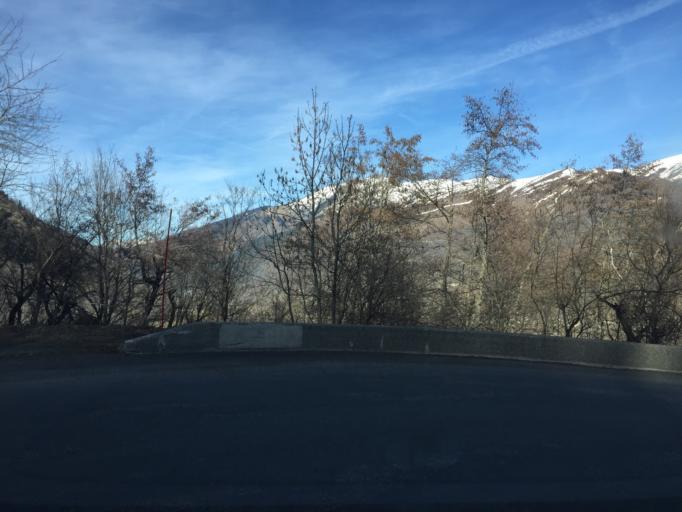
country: FR
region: Midi-Pyrenees
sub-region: Departement des Hautes-Pyrenees
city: Saint-Lary-Soulan
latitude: 42.8037
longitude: 0.3985
